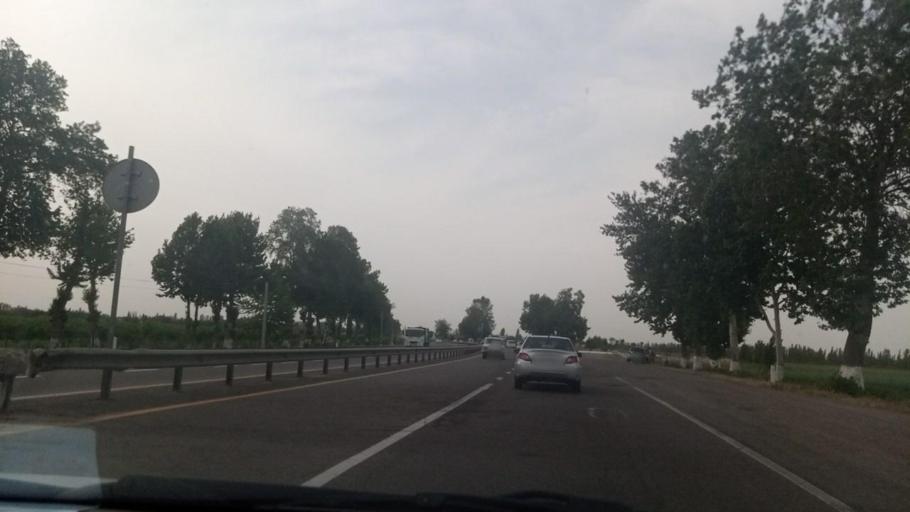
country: UZ
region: Toshkent Shahri
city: Bektemir
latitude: 41.1427
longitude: 69.4326
